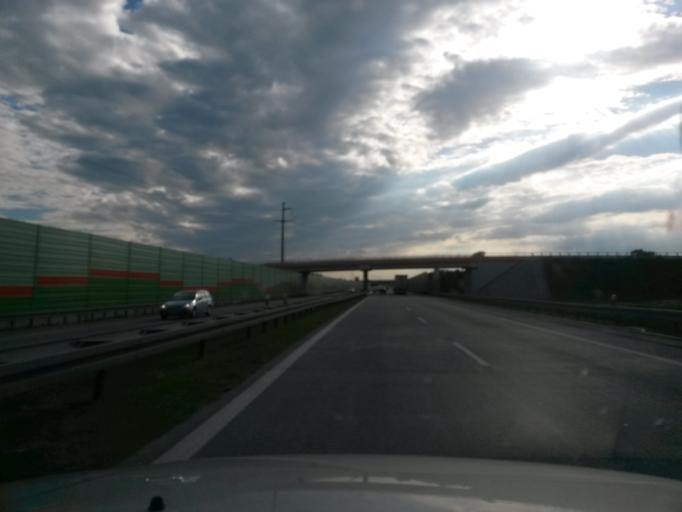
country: PL
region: Lodz Voivodeship
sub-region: Piotrkow Trybunalski
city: Piotrkow Trybunalski
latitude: 51.4450
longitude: 19.7494
